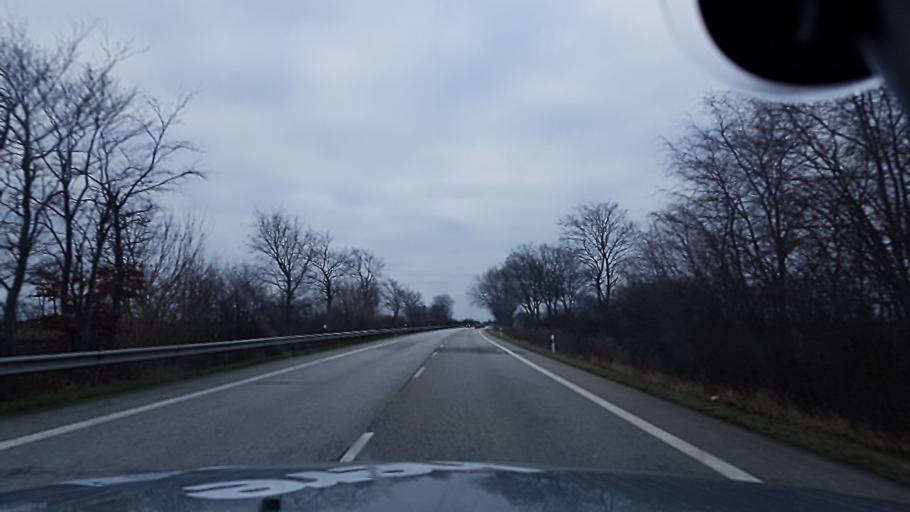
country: DE
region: Schleswig-Holstein
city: Fehmarn
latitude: 54.4570
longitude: 11.1916
